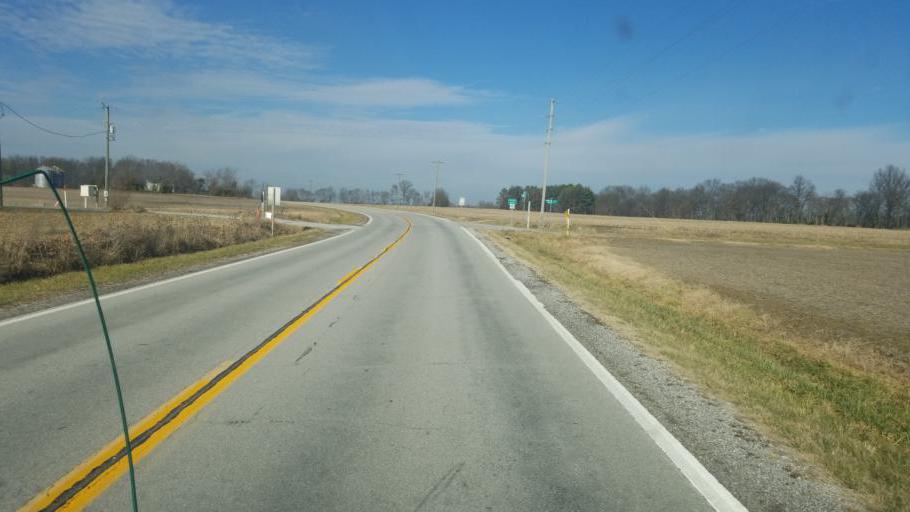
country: US
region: Illinois
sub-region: Saline County
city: Eldorado
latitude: 37.9066
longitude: -88.4531
